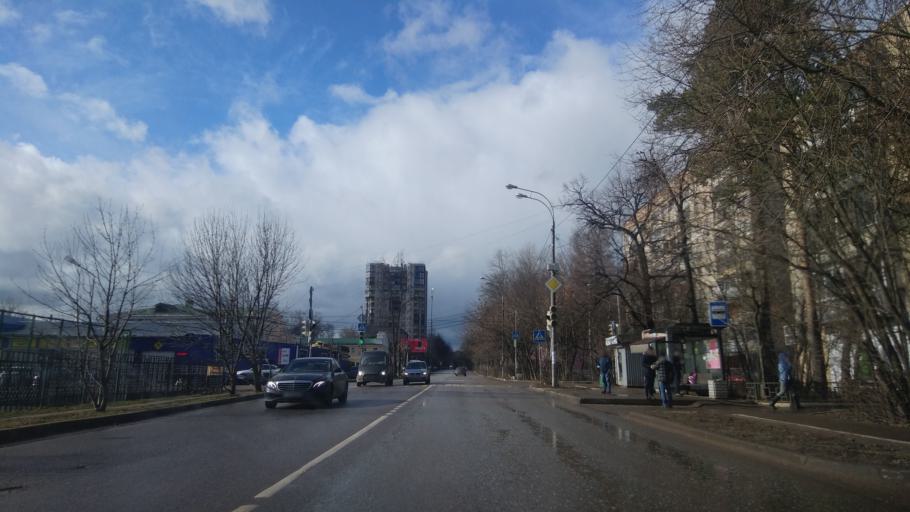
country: RU
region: Moskovskaya
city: Pushkino
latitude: 56.0012
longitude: 37.8522
